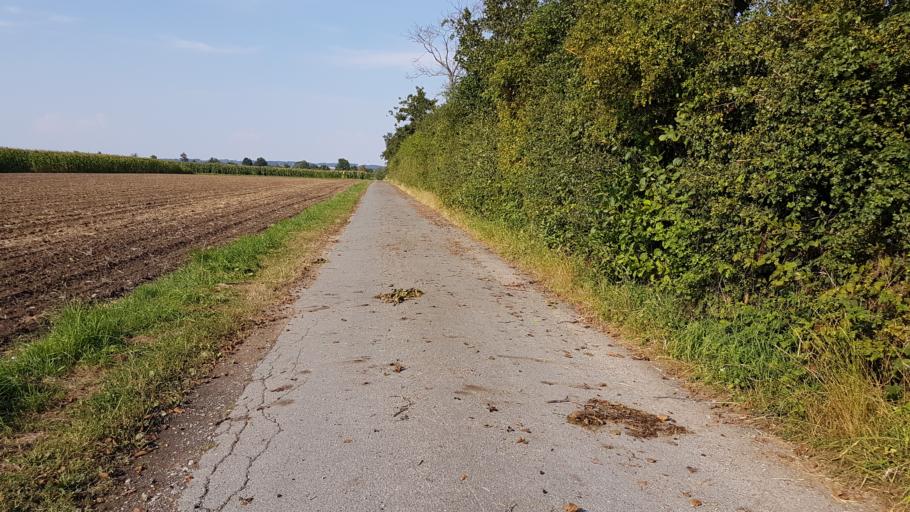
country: DE
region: North Rhine-Westphalia
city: Olfen
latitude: 51.6955
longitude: 7.3706
